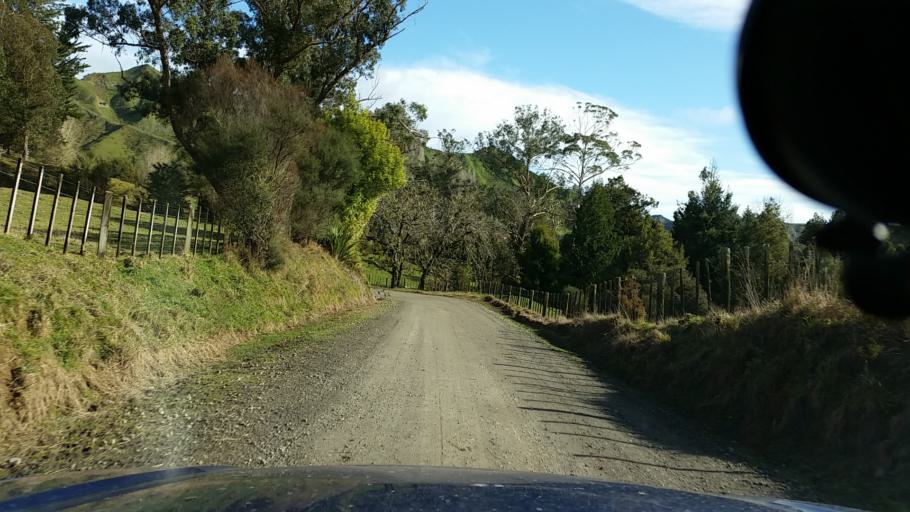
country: NZ
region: Taranaki
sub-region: New Plymouth District
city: Waitara
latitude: -39.0587
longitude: 174.7807
